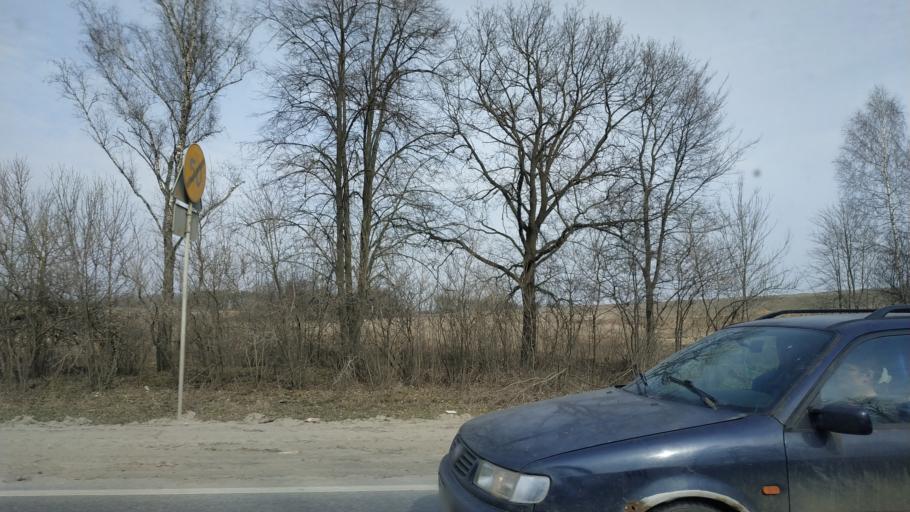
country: RU
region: Moskovskaya
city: Bronnitsy
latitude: 55.3888
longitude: 38.3374
